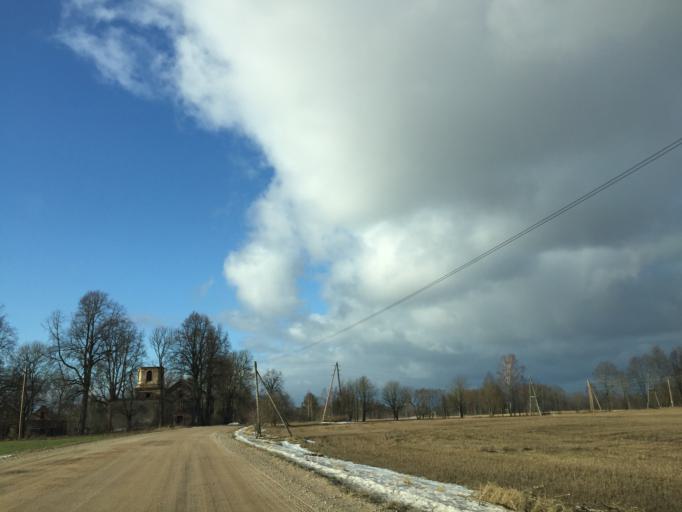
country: LV
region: Limbazu Rajons
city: Limbazi
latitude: 57.6167
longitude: 24.5805
